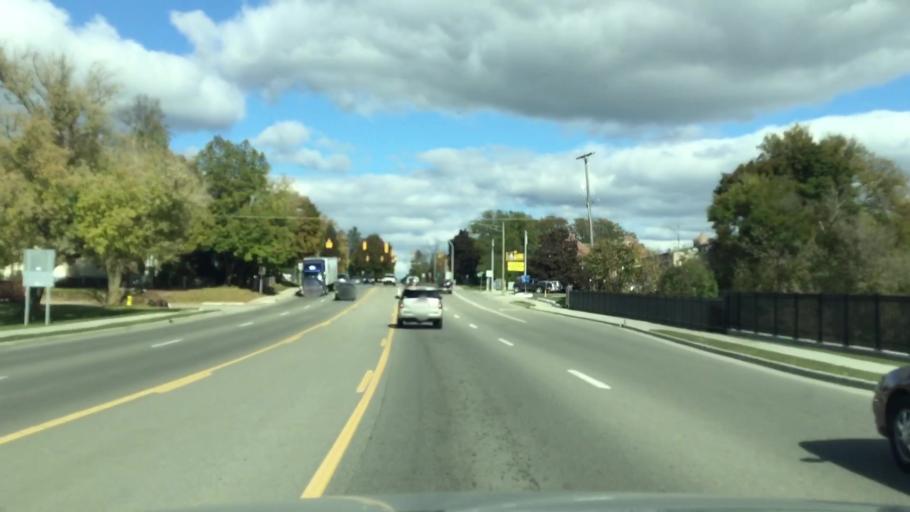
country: US
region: Michigan
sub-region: Lapeer County
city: Lapeer
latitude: 43.0493
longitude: -83.3185
